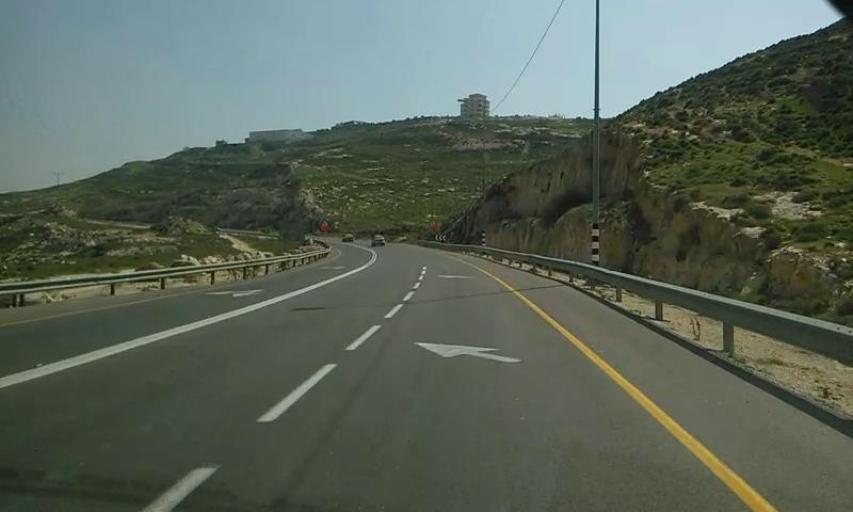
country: PS
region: West Bank
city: Jaba`
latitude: 31.8625
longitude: 35.2603
